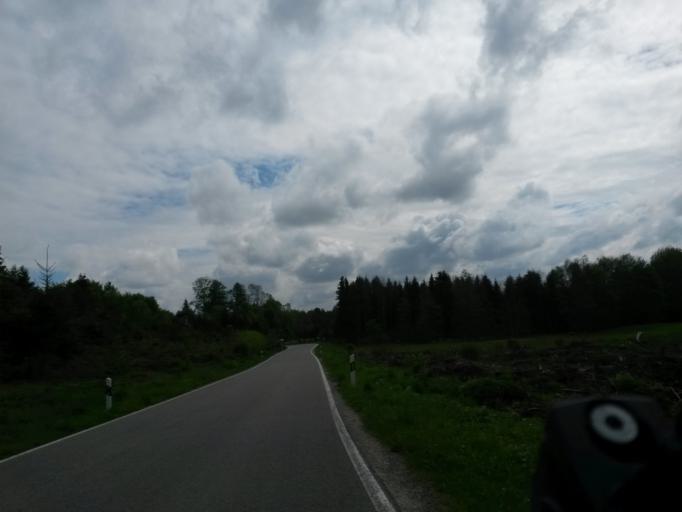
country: DE
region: Baden-Wuerttemberg
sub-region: Tuebingen Region
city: Bergatreute
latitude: 47.8744
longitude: 9.7174
